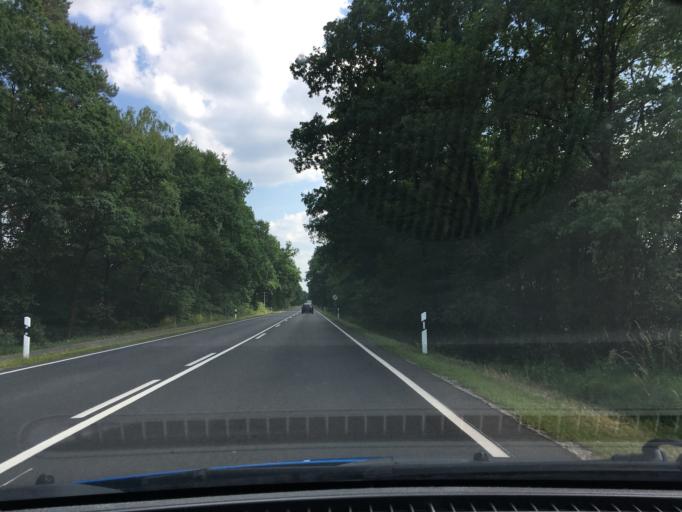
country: DE
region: Lower Saxony
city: Welle
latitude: 53.1999
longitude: 9.8265
